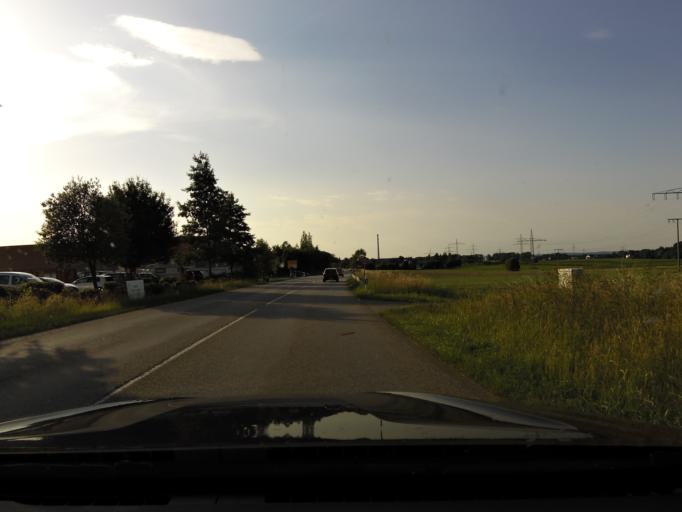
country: DE
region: Bavaria
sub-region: Upper Bavaria
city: Burgkirchen an der Alz
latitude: 48.1577
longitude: 12.7434
